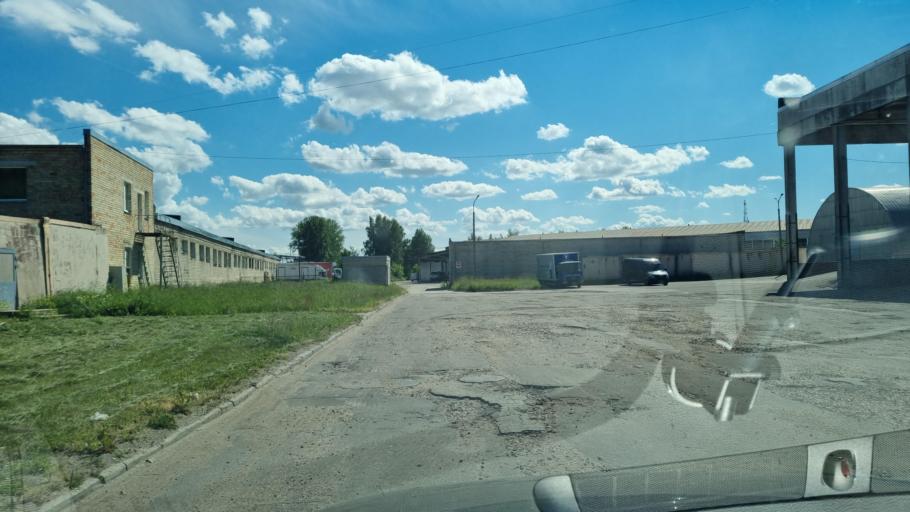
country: LV
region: Riga
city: Bolderaja
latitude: 56.9727
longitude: 24.0366
